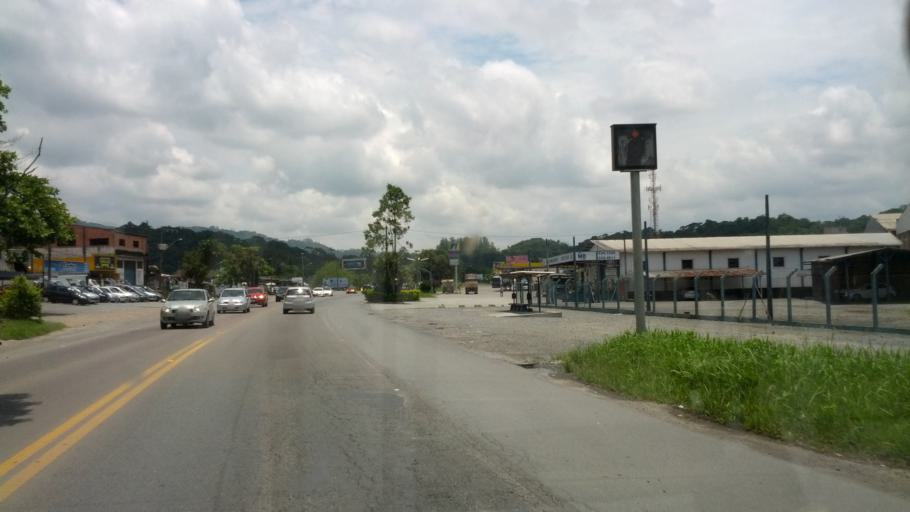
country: BR
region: Santa Catarina
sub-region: Blumenau
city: Blumenau
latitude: -26.8815
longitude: -49.1381
